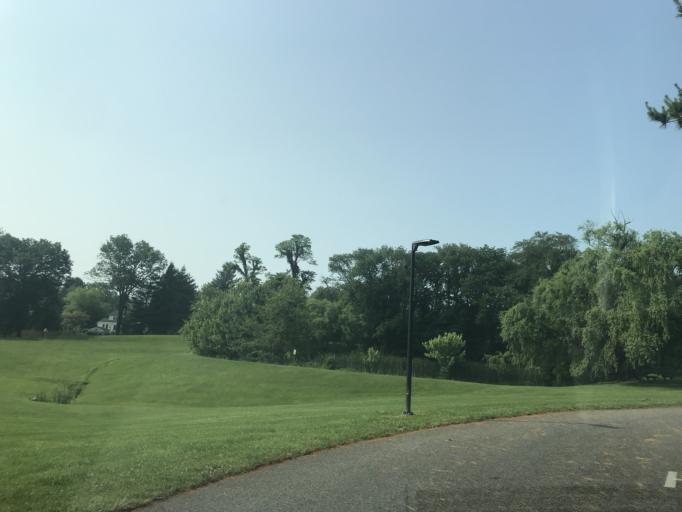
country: US
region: Maryland
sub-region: Harford County
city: South Bel Air
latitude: 39.5364
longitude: -76.3334
